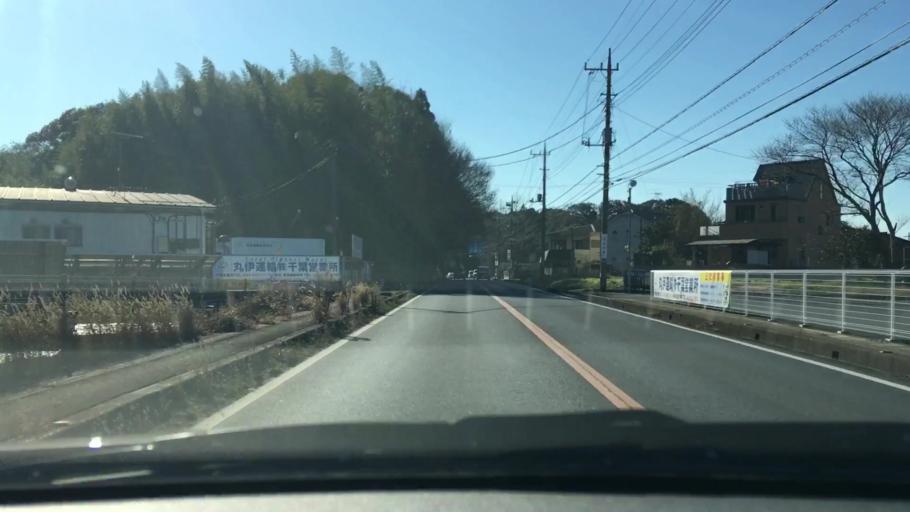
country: JP
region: Chiba
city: Shisui
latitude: 35.7014
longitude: 140.3107
